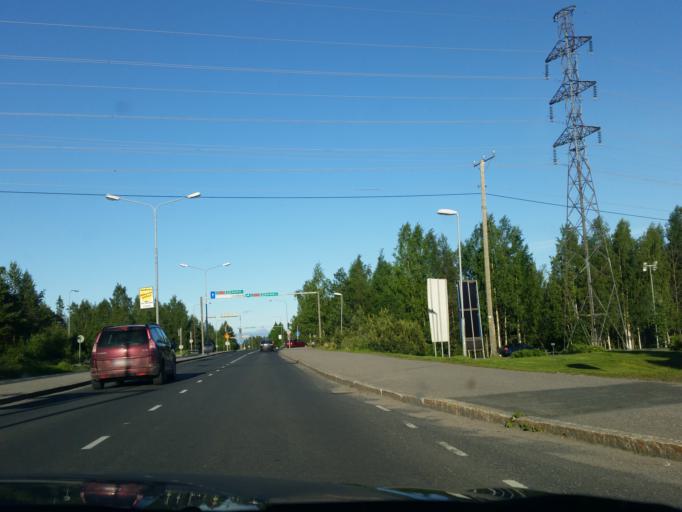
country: FI
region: Northern Savo
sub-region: Kuopio
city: Kuopio
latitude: 62.8623
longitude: 27.6151
